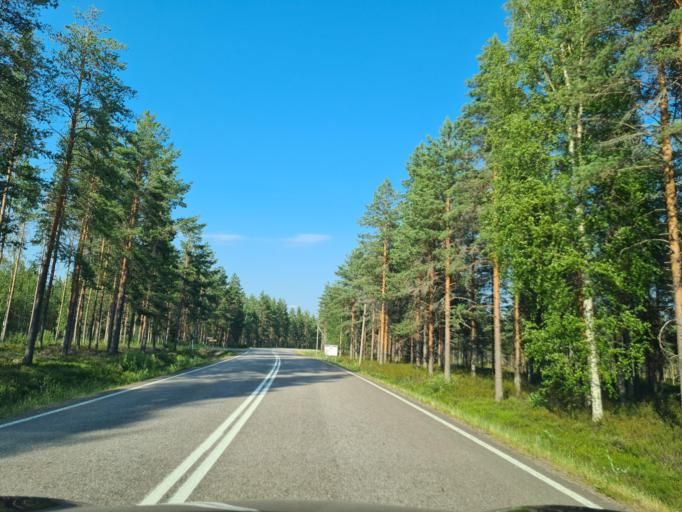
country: FI
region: Satakunta
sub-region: Pohjois-Satakunta
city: Karvia
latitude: 62.3243
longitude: 22.6836
